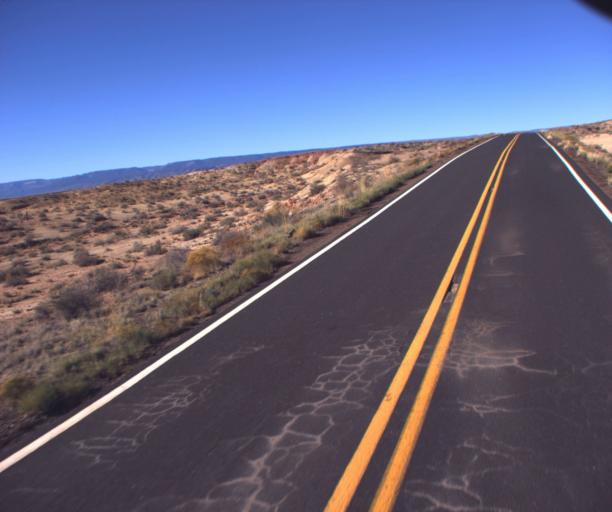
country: US
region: Arizona
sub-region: Coconino County
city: Page
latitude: 36.6841
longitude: -111.8443
